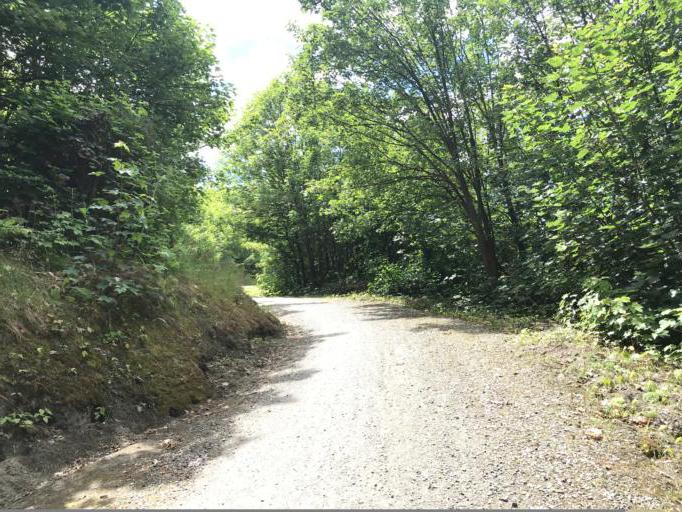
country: NZ
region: Otago
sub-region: Queenstown-Lakes District
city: Arrowtown
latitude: -45.0090
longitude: 168.8958
